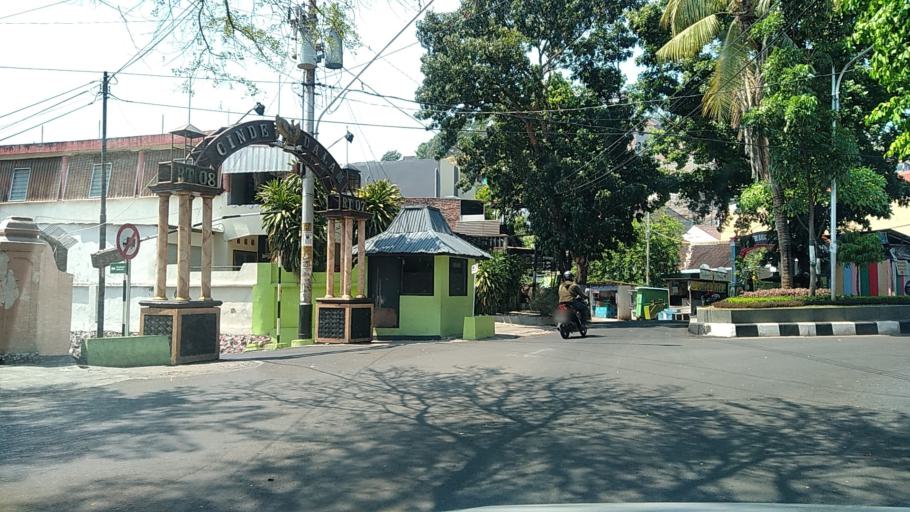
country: ID
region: Central Java
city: Semarang
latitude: -7.0116
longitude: 110.4366
